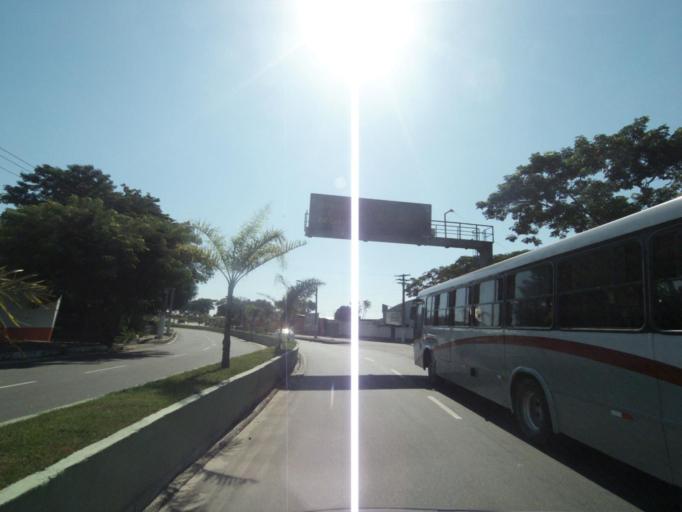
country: BR
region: Rio de Janeiro
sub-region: Niteroi
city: Niteroi
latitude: -22.8597
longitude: -43.1030
